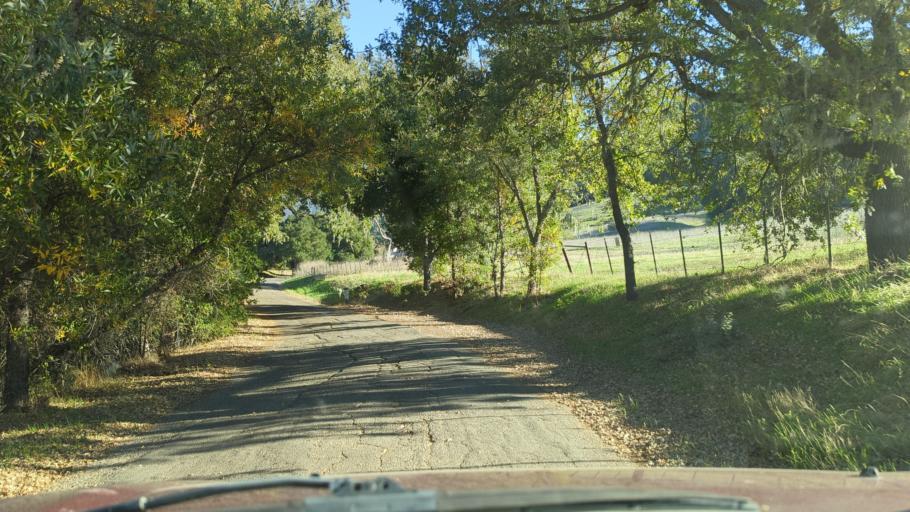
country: US
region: California
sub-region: Santa Barbara County
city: Santa Ynez
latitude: 34.5647
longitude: -120.0926
